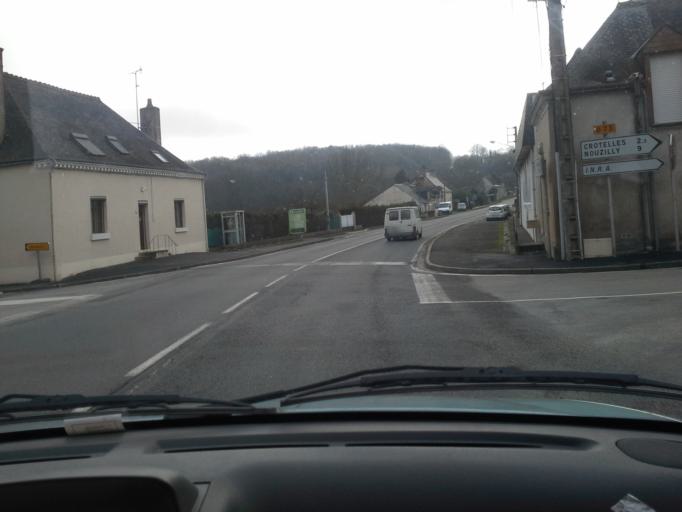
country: FR
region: Centre
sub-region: Departement d'Indre-et-Loire
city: Villedomer
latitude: 47.5490
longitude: 0.8636
